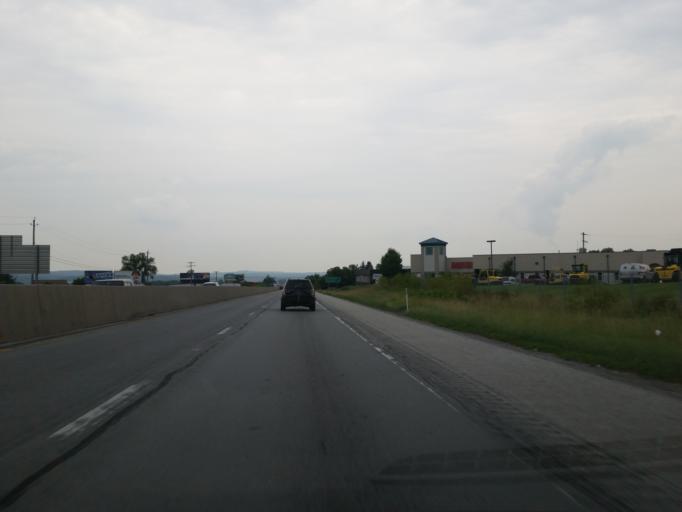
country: US
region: Pennsylvania
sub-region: York County
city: Emigsville
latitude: 40.0280
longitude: -76.7447
